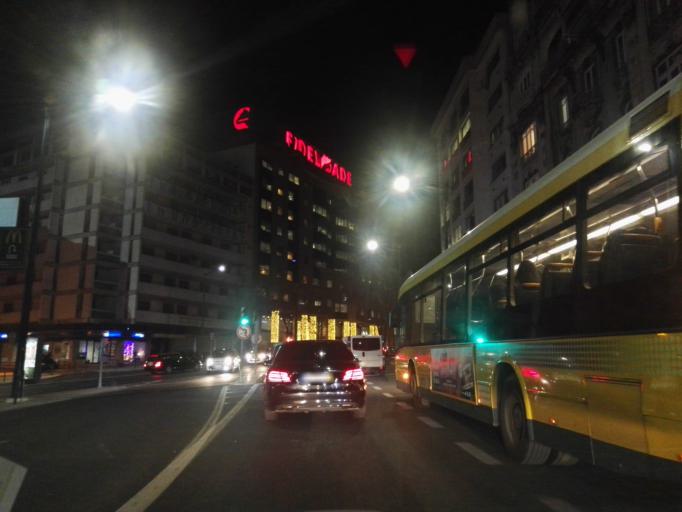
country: PT
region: Lisbon
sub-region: Lisbon
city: Lisbon
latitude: 38.7216
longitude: -9.1524
